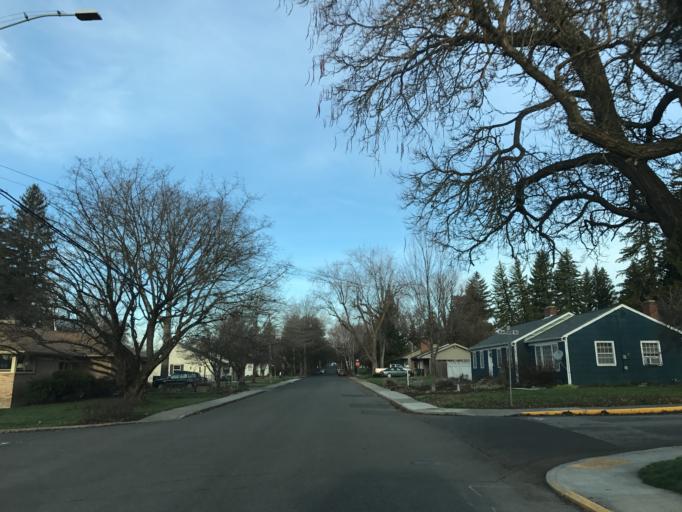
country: US
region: Idaho
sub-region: Latah County
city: Moscow
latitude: 46.7355
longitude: -116.9869
